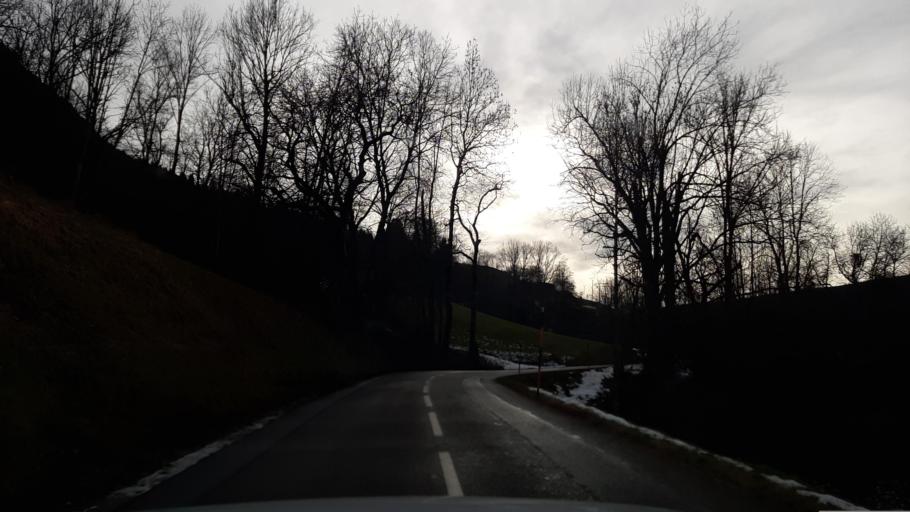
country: FR
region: Rhone-Alpes
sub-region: Departement de la Haute-Savoie
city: Cusy
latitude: 45.6668
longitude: 6.1010
